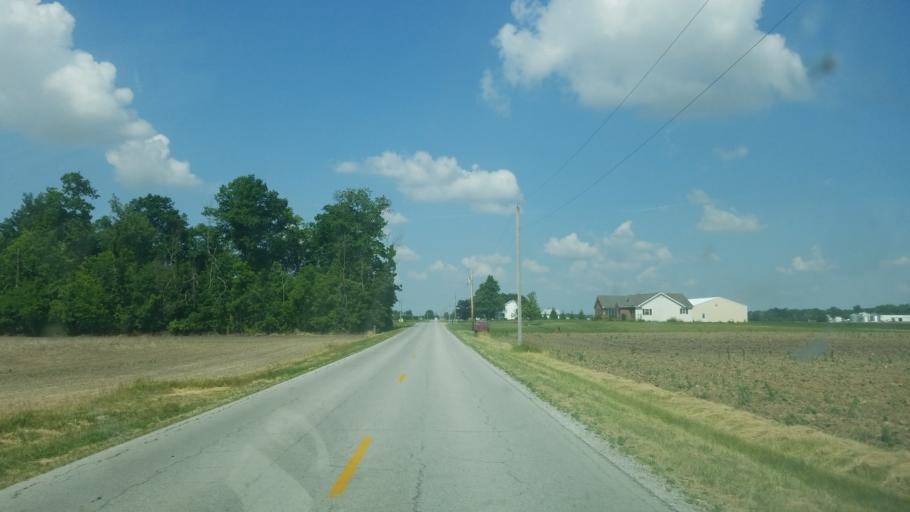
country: US
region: Ohio
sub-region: Auglaize County
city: Wapakoneta
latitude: 40.5703
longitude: -84.1347
